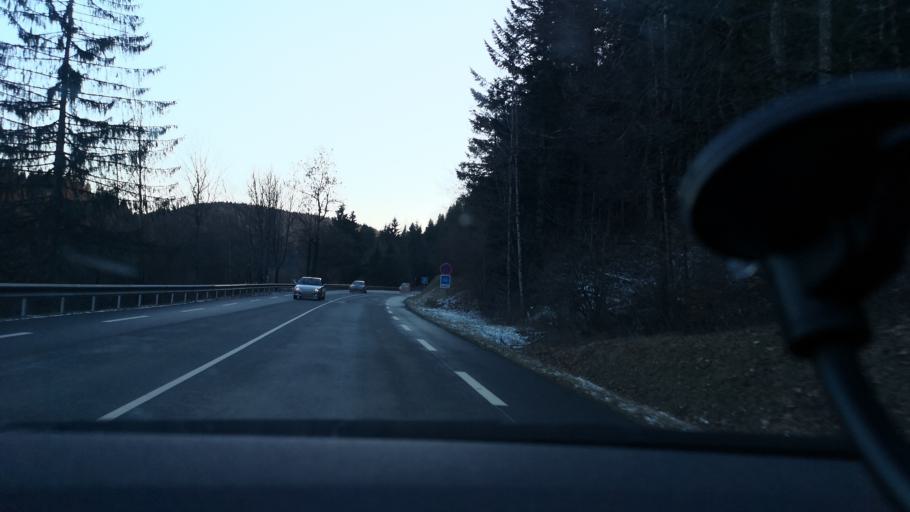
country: FR
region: Franche-Comte
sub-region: Departement du Doubs
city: La Cluse-et-Mijoux
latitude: 46.8740
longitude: 6.3662
